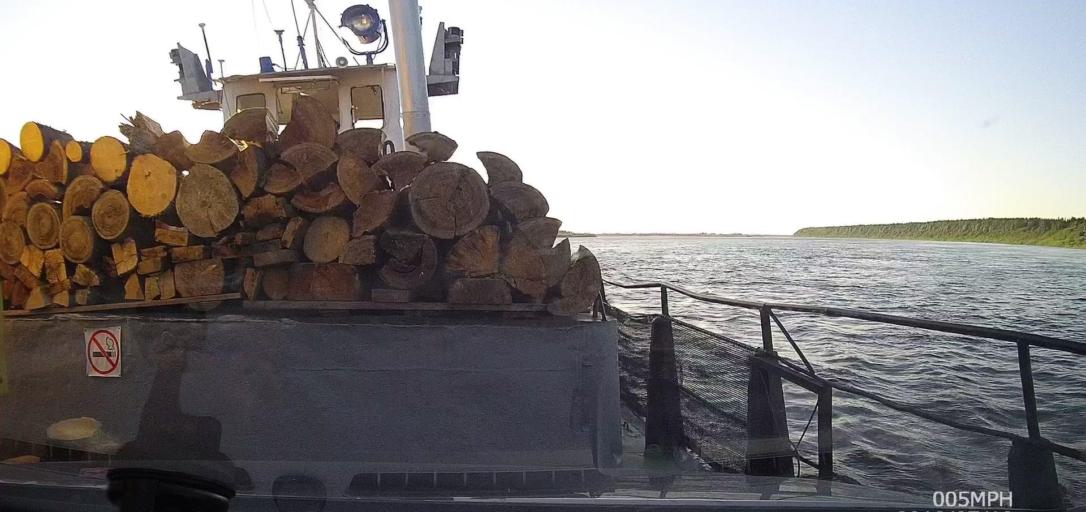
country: RU
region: Arkhangelskaya
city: Lukovetskiy
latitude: 64.1576
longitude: 41.9189
